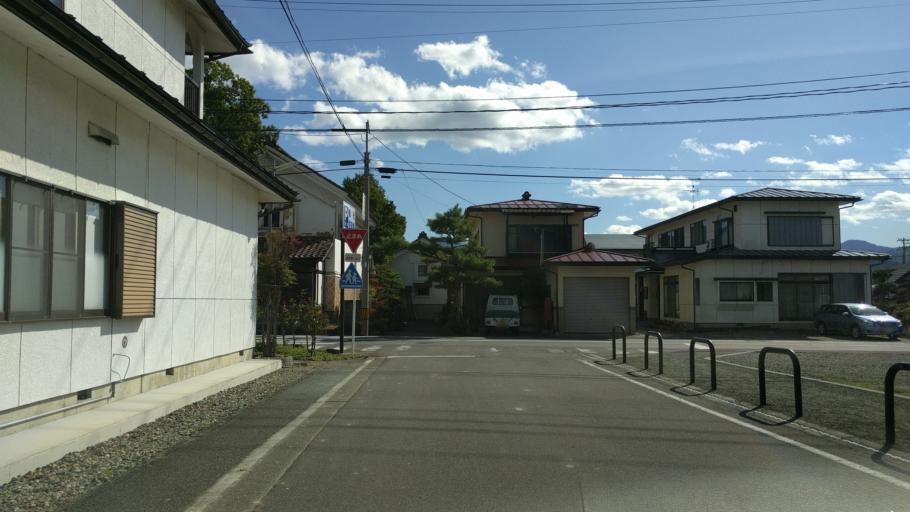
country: JP
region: Fukushima
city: Kitakata
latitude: 37.4507
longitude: 139.8885
